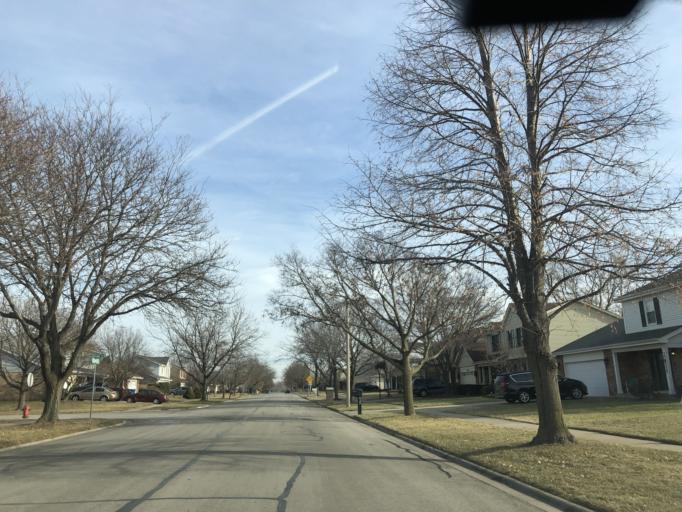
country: US
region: Illinois
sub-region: DuPage County
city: Woodridge
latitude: 41.7173
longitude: -88.0257
